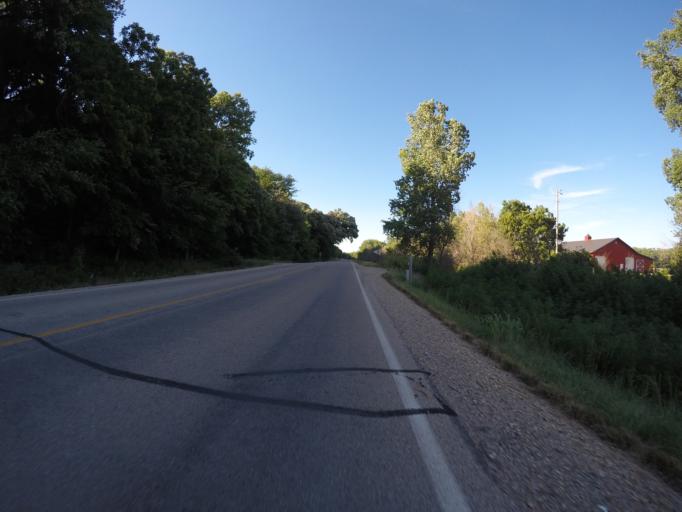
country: US
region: Kansas
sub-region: Riley County
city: Manhattan
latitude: 39.1554
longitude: -96.5973
